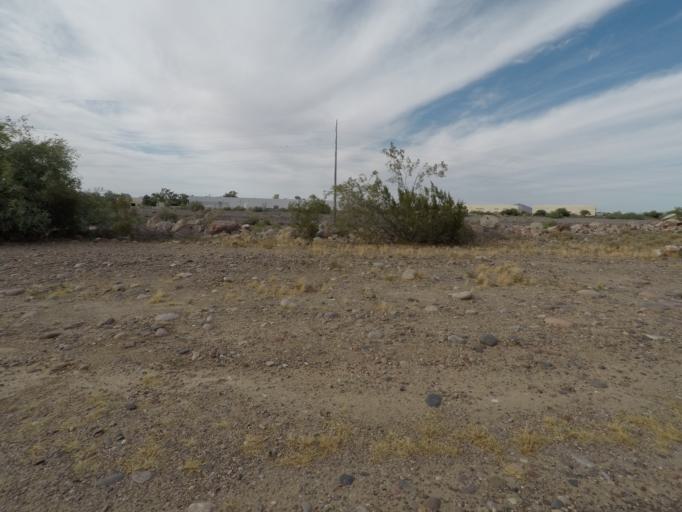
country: US
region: Arizona
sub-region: Maricopa County
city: Phoenix
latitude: 33.4197
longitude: -112.0596
